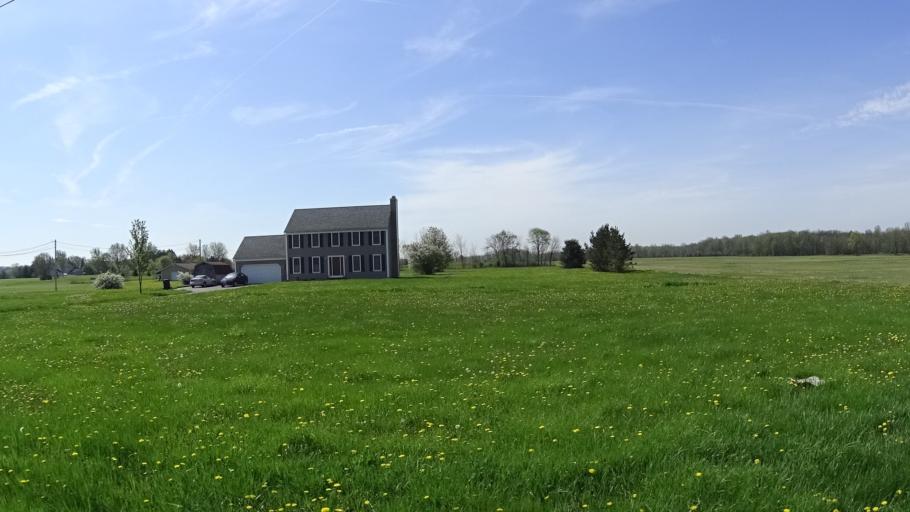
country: US
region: Ohio
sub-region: Lorain County
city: Lagrange
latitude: 41.2747
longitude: -82.1425
